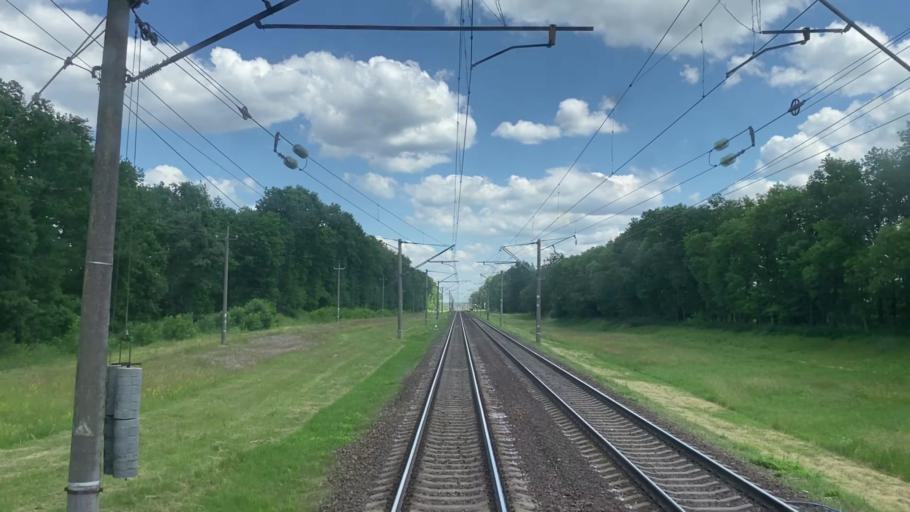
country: BY
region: Brest
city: Byaroza
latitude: 52.5457
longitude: 24.9627
